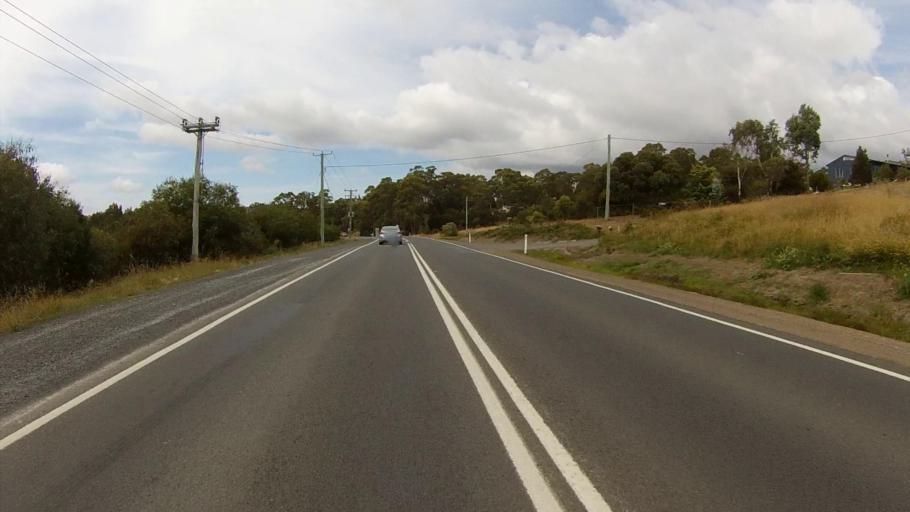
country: AU
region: Tasmania
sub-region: Kingborough
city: Margate
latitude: -43.0371
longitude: 147.2661
